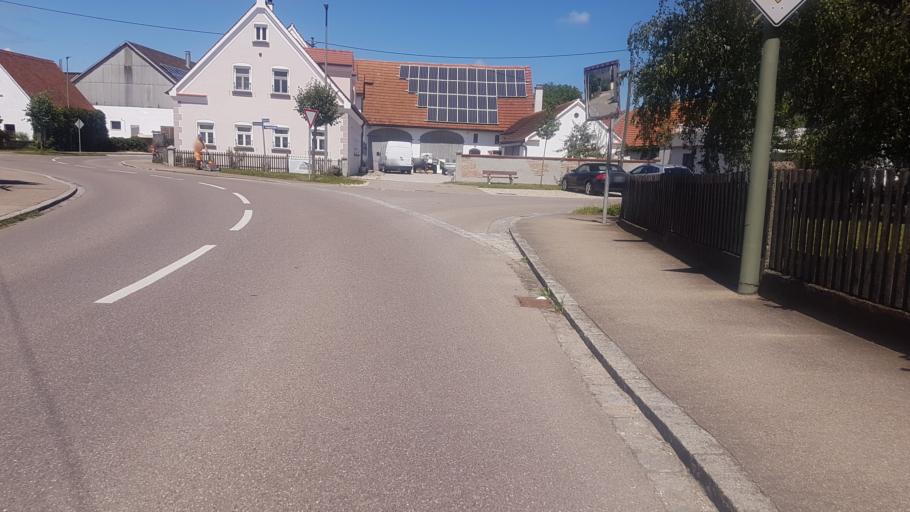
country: DE
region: Bavaria
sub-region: Swabia
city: Blindheim
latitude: 48.6316
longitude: 10.6185
